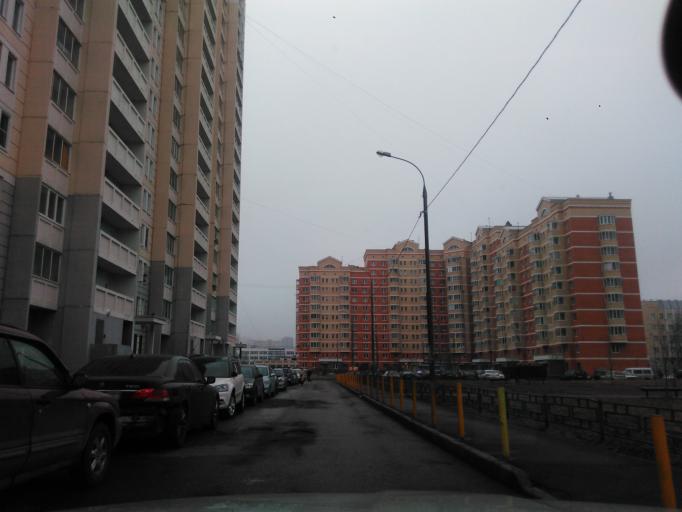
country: RU
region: Moscow
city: Zelenograd
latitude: 55.9755
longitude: 37.1657
